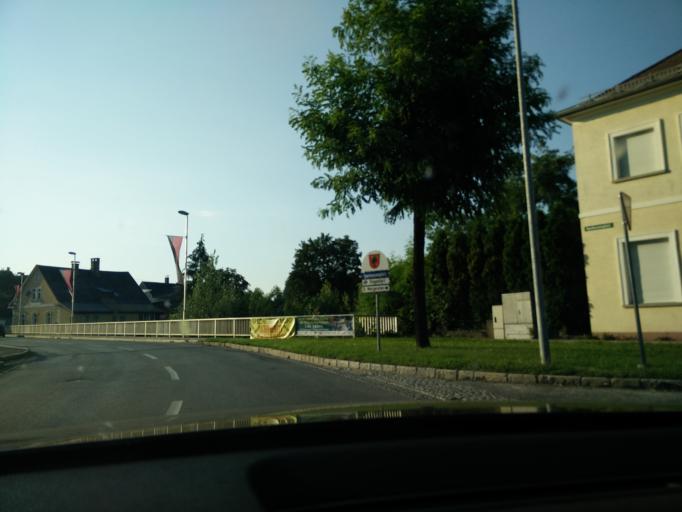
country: AT
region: Carinthia
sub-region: Politischer Bezirk Klagenfurt Land
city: Ferlach
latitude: 46.5270
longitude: 14.2981
